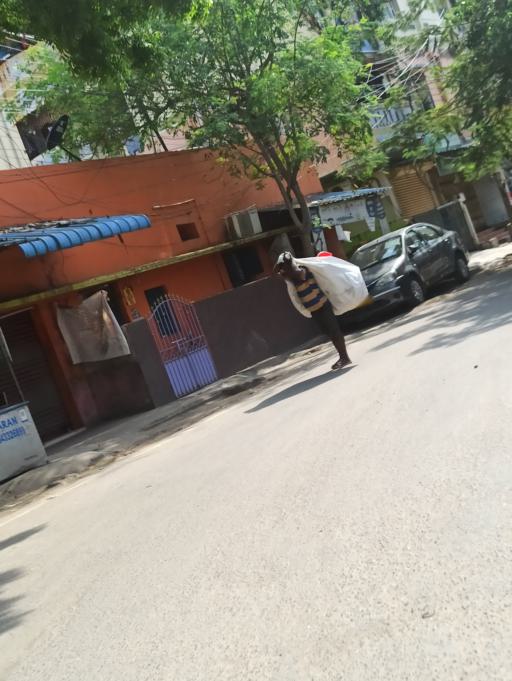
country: IN
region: Tamil Nadu
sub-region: Chennai
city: Chetput
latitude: 13.0599
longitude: 80.2232
